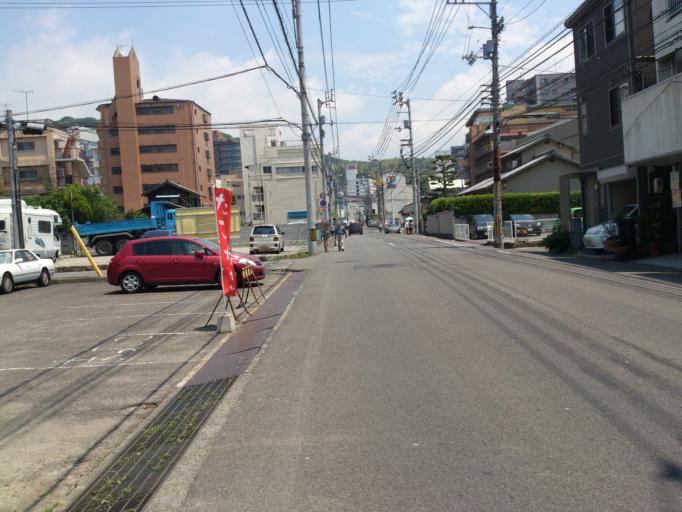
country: JP
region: Ehime
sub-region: Shikoku-chuo Shi
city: Matsuyama
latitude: 33.8523
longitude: 132.7815
